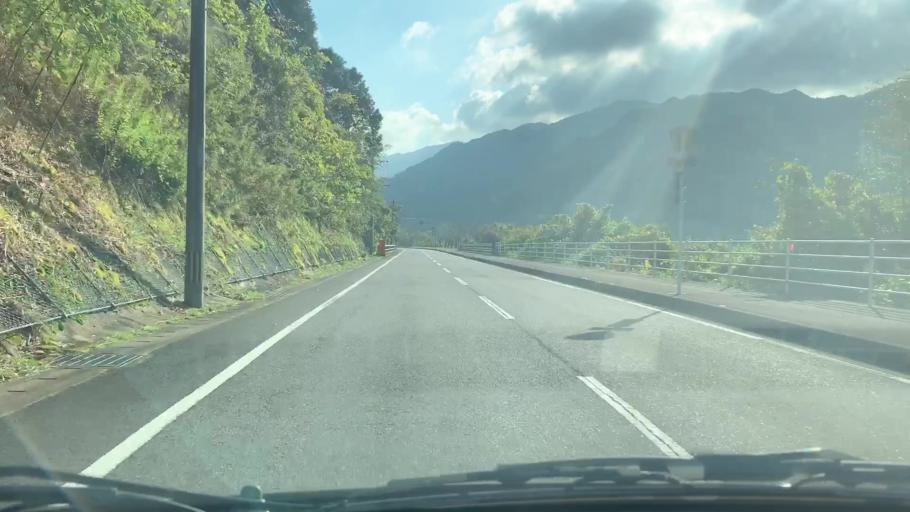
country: JP
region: Saga Prefecture
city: Kashima
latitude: 33.0381
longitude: 130.0710
